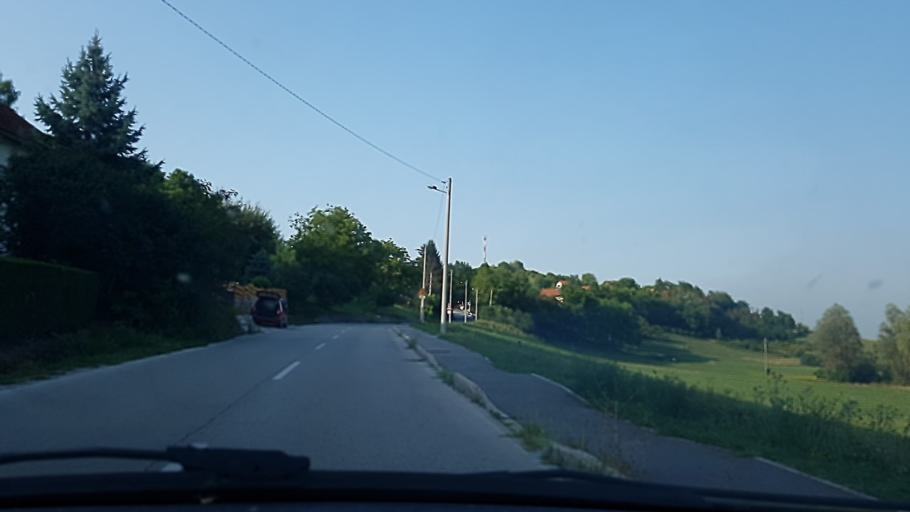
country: HR
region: Zagrebacka
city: Pojatno
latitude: 45.9219
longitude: 15.8078
